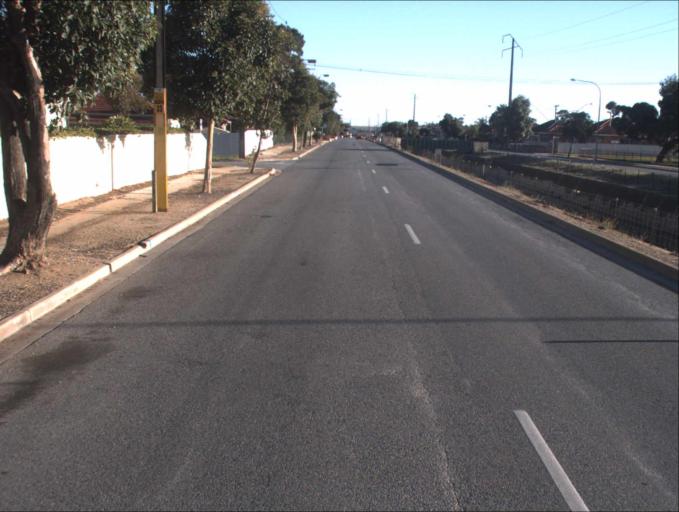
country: AU
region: South Australia
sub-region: Port Adelaide Enfield
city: Alberton
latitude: -34.8486
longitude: 138.5350
